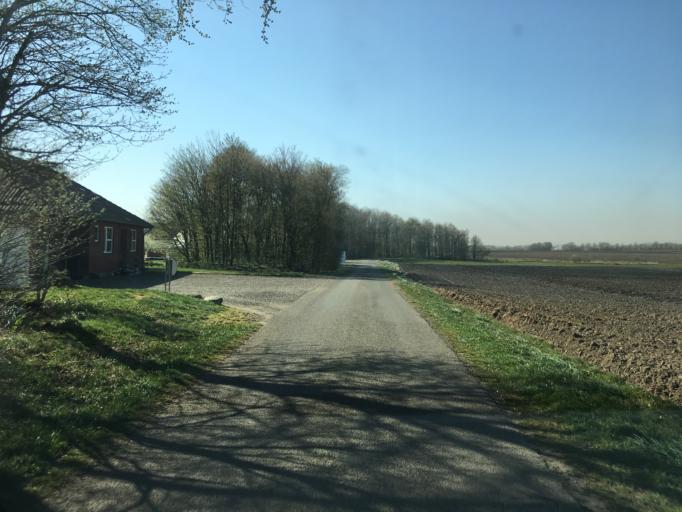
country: DK
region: South Denmark
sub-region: Aabenraa Kommune
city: Rodekro
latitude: 55.1109
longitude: 9.2008
